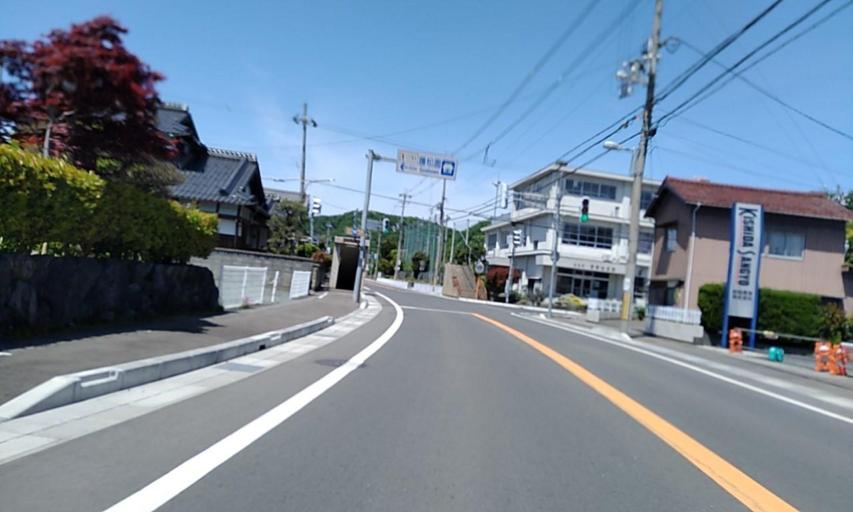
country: JP
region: Fukui
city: Obama
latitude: 35.5124
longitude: 135.7528
